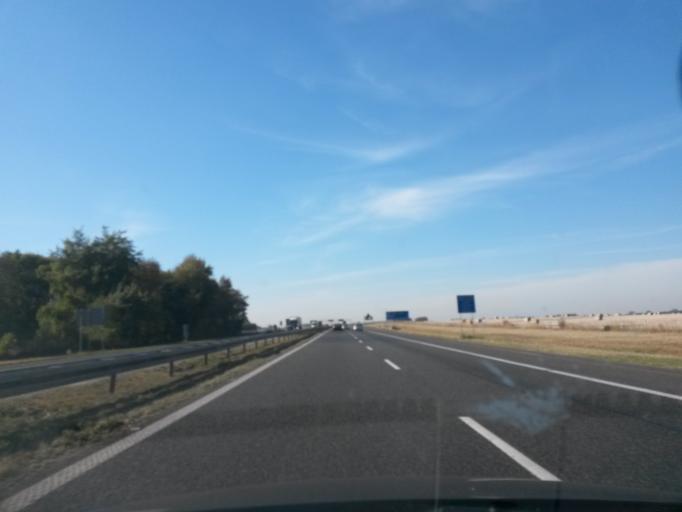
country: PL
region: Opole Voivodeship
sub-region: Powiat brzeski
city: Grodkow
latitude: 50.7843
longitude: 17.3446
